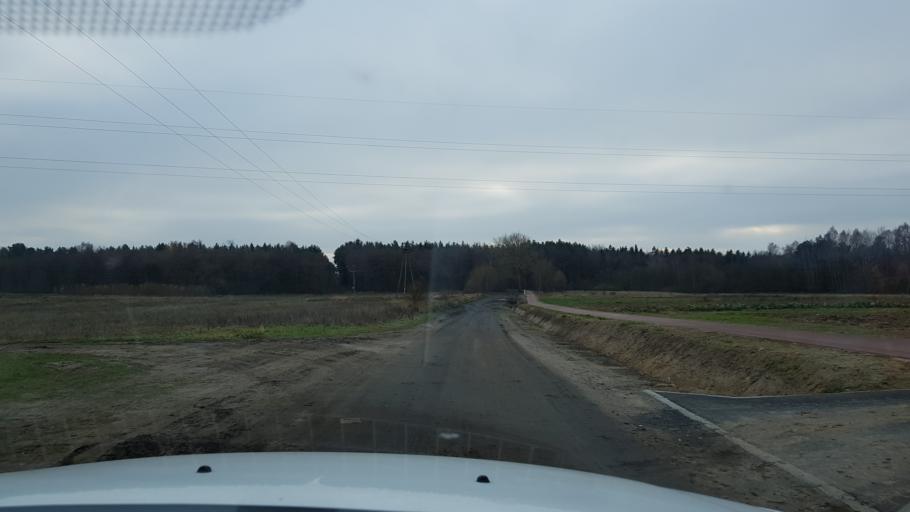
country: PL
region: West Pomeranian Voivodeship
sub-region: Powiat kolobrzeski
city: Grzybowo
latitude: 54.1376
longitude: 15.5143
